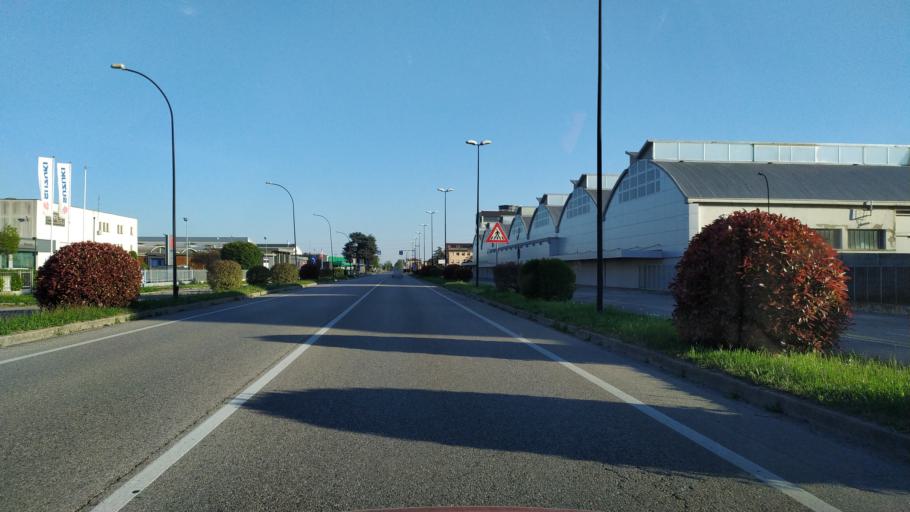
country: IT
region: Veneto
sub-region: Provincia di Padova
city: Limena
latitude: 45.4610
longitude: 11.8537
